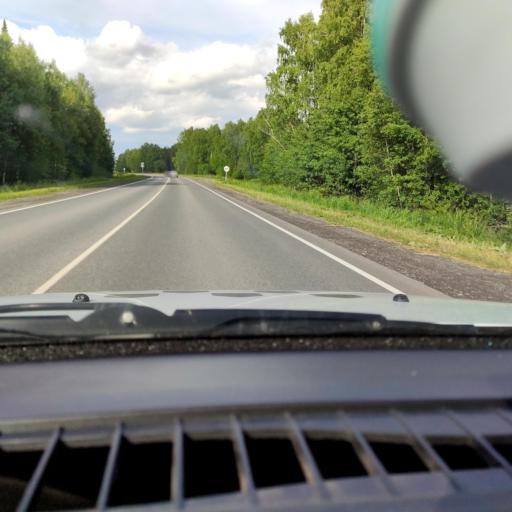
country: RU
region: Perm
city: Orda
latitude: 57.2472
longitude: 56.9949
